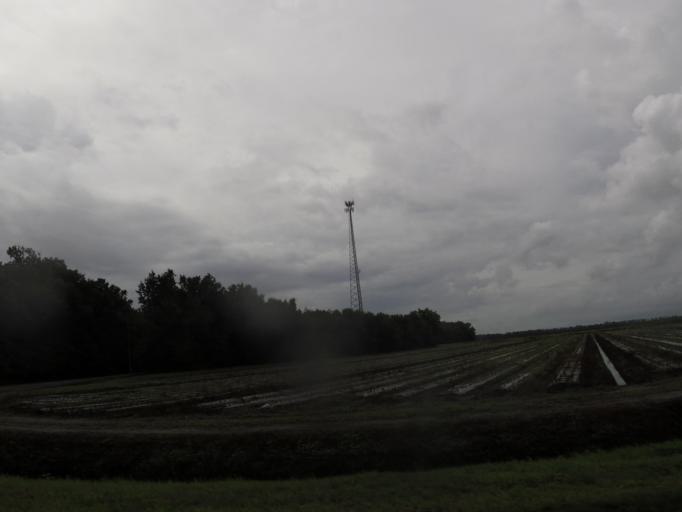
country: US
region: Florida
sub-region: Putnam County
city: East Palatka
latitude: 29.8504
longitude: -81.5234
